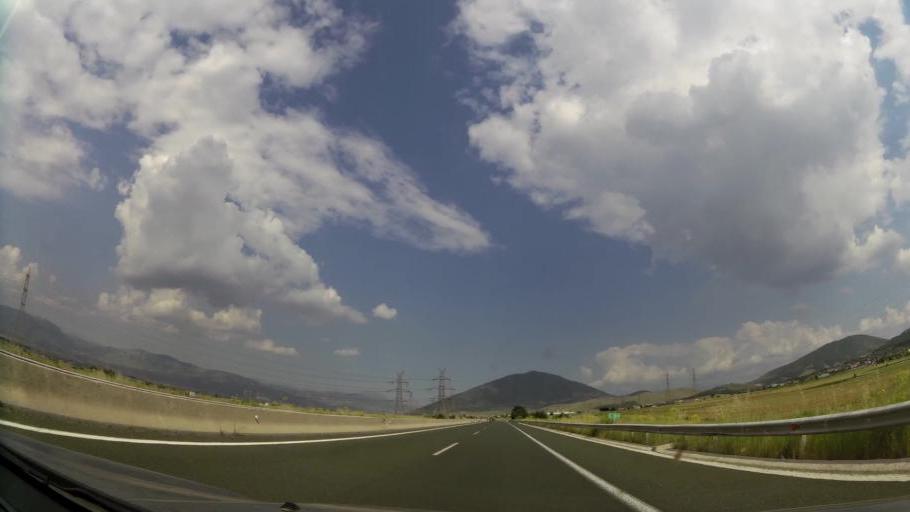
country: GR
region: West Macedonia
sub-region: Nomos Kozanis
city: Koila
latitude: 40.3619
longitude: 21.8282
